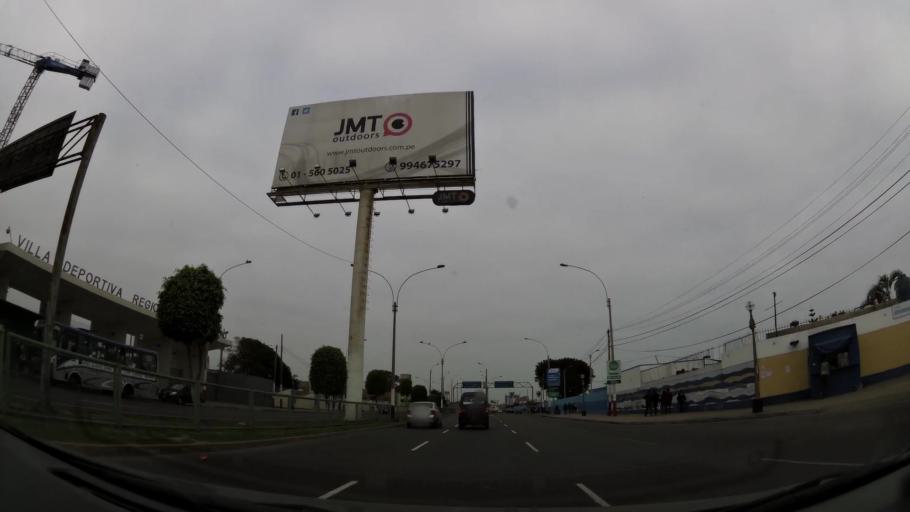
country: PE
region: Callao
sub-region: Callao
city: Callao
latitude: -12.0633
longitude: -77.1223
